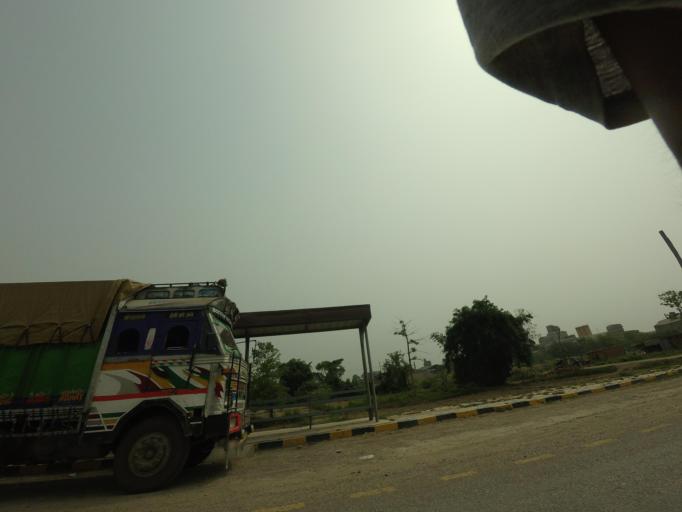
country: NP
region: Western Region
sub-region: Lumbini Zone
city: Bhairahawa
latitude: 27.5054
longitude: 83.3696
